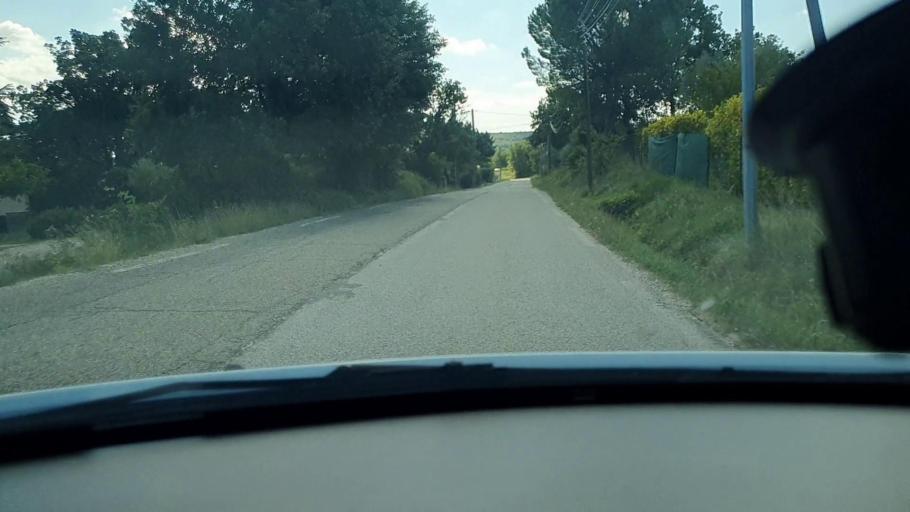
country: FR
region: Languedoc-Roussillon
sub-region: Departement du Gard
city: Sabran
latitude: 44.1494
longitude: 4.4893
